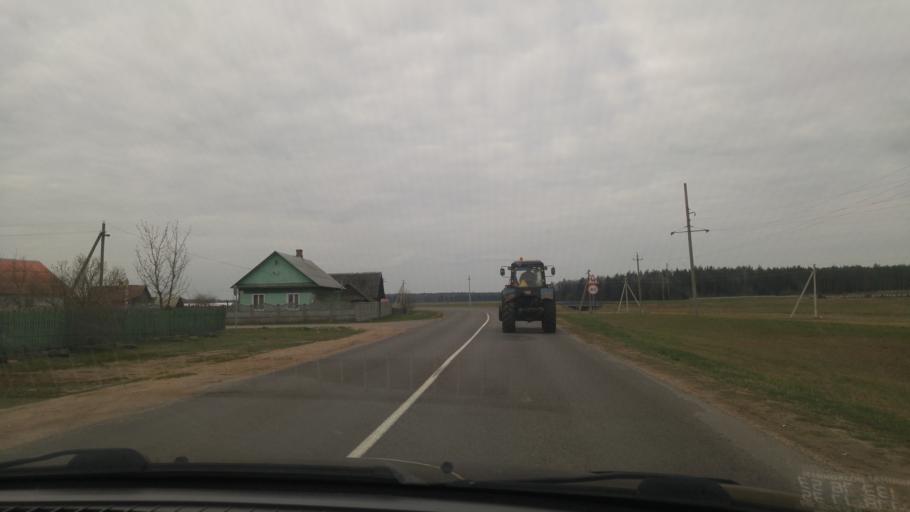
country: BY
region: Minsk
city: Chervyen'
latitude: 53.7197
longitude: 28.3814
